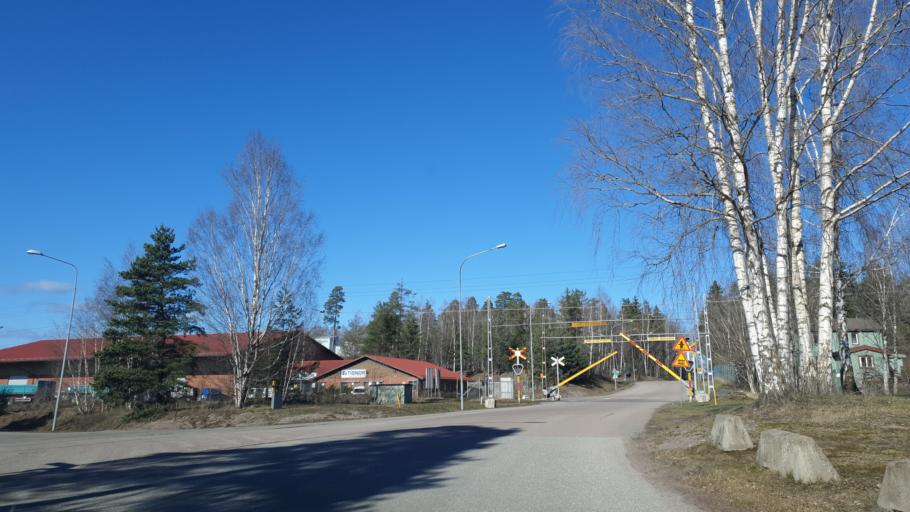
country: SE
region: Vaestmanland
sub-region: Kopings Kommun
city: Koping
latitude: 59.4994
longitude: 16.0383
